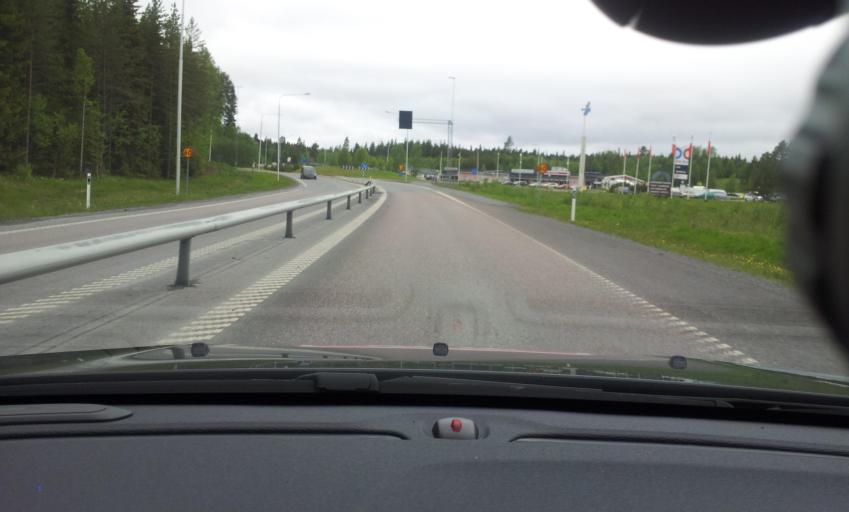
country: SE
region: Jaemtland
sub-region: Krokoms Kommun
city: Krokom
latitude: 63.3268
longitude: 14.4324
